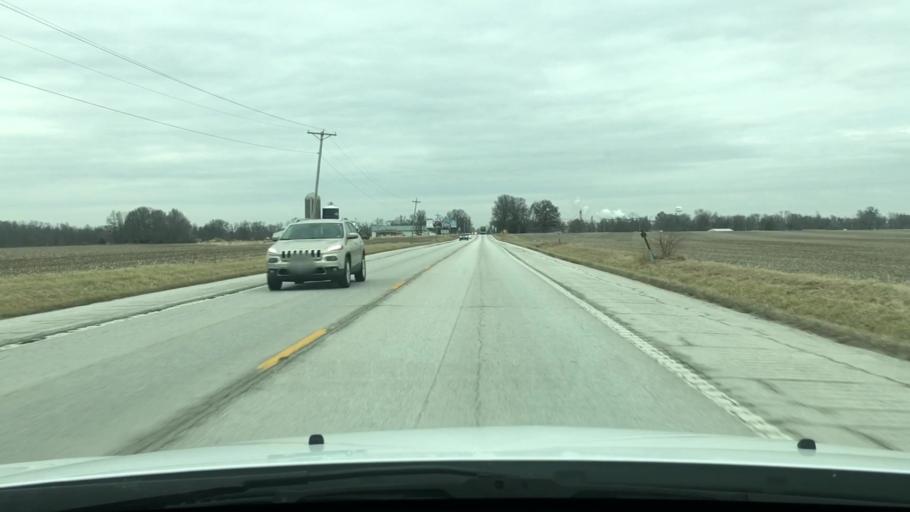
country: US
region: Missouri
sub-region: Montgomery County
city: Wellsville
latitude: 39.2309
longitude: -91.6459
